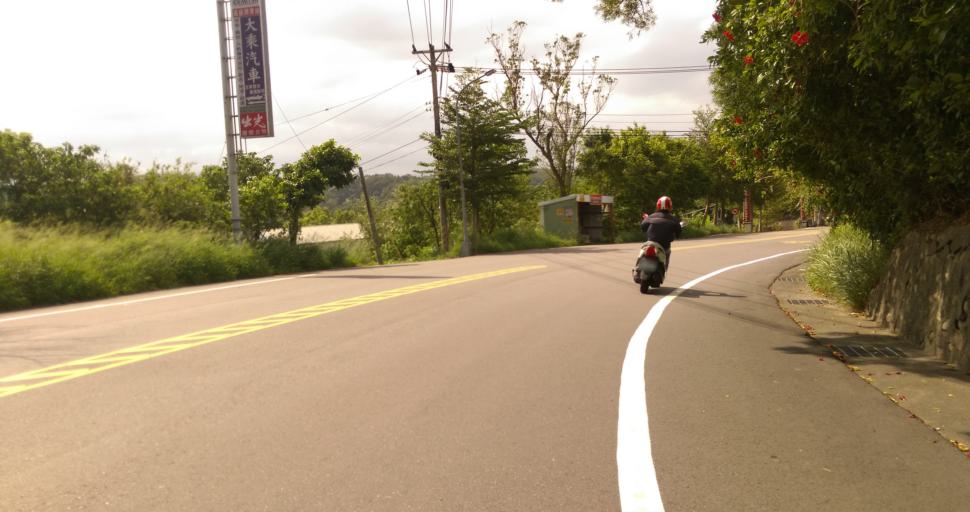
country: TW
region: Taiwan
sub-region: Hsinchu
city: Hsinchu
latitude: 24.7633
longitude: 120.9623
